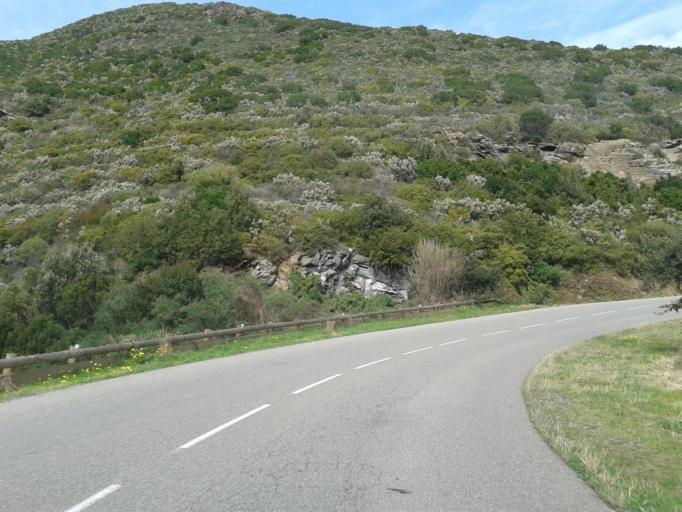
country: FR
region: Corsica
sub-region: Departement de la Haute-Corse
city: Brando
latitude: 42.8602
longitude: 9.4793
